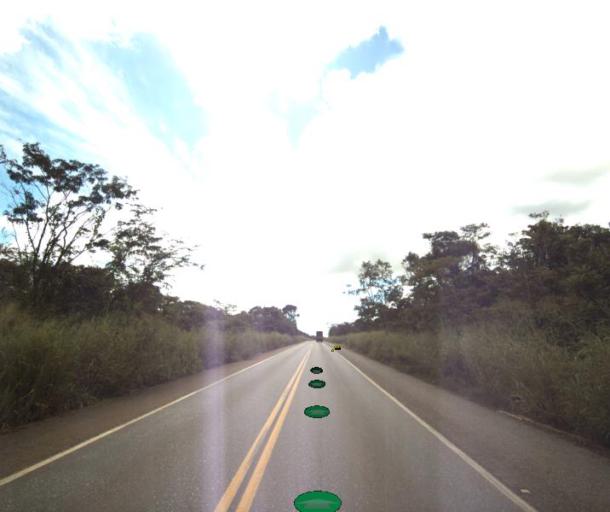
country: BR
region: Goias
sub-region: Jaragua
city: Jaragua
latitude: -15.9028
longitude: -49.2309
